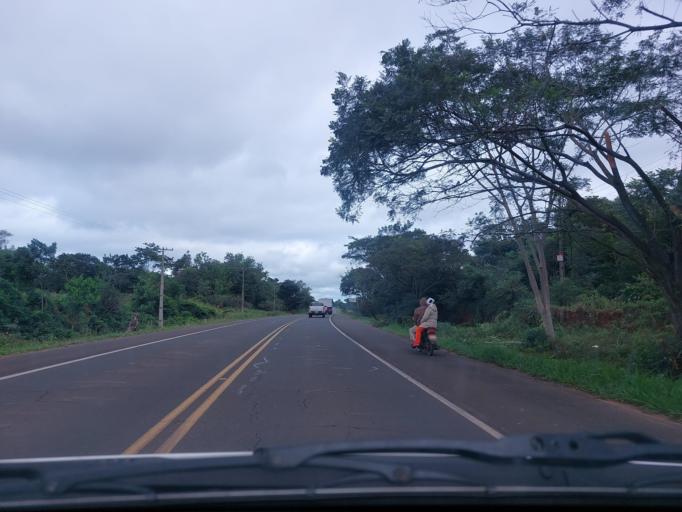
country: PY
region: San Pedro
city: Guayaybi
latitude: -24.6468
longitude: -56.3797
